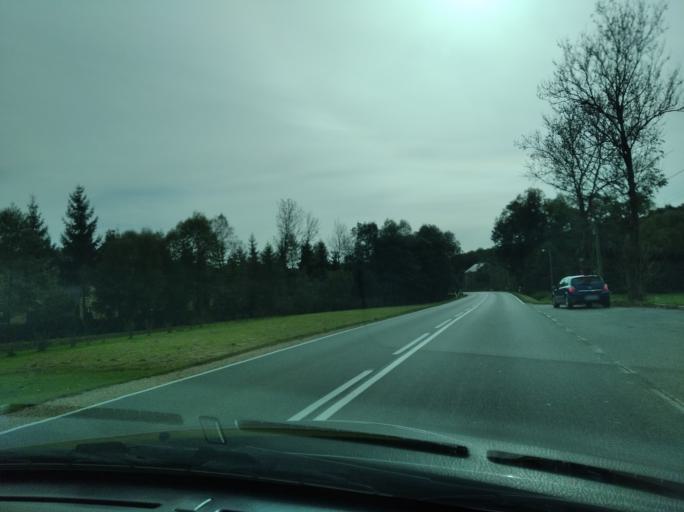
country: PL
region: Subcarpathian Voivodeship
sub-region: Powiat strzyzowski
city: Wisniowa
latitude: 49.8906
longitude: 21.6438
